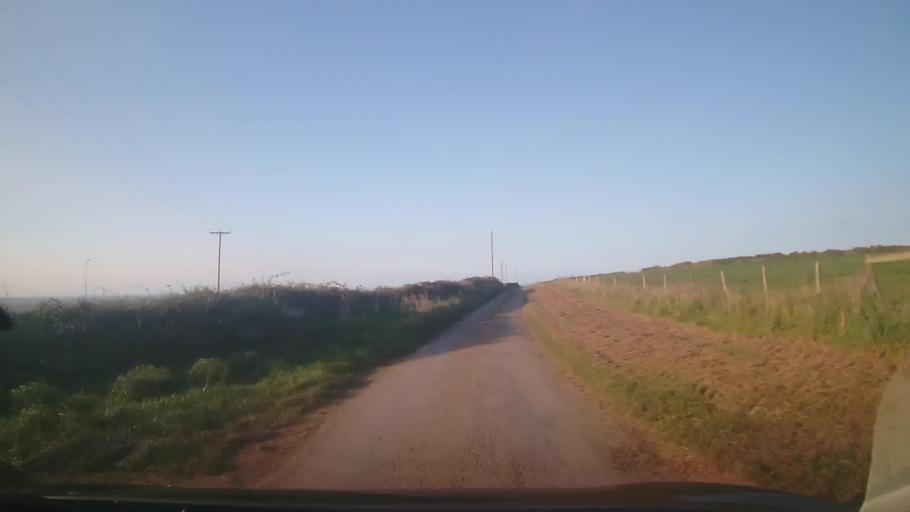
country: GB
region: Wales
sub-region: Pembrokeshire
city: Llanrhian
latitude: 51.9236
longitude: -5.2186
